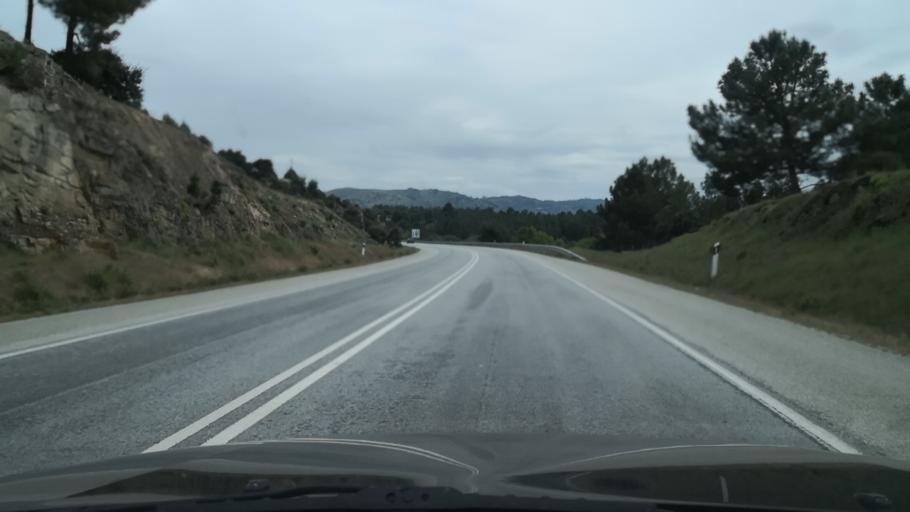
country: PT
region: Guarda
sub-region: Celorico da Beira
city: Celorico da Beira
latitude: 40.6374
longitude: -7.3228
